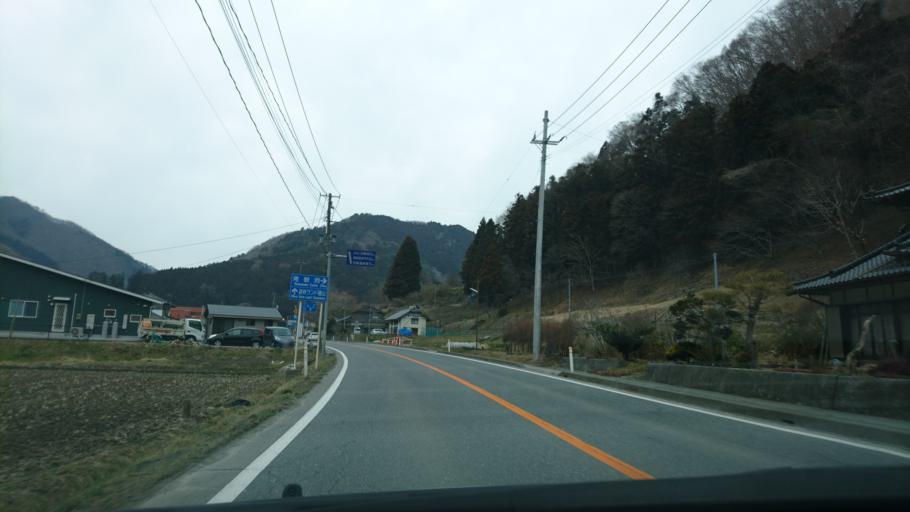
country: JP
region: Iwate
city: Tono
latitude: 39.1501
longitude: 141.5437
